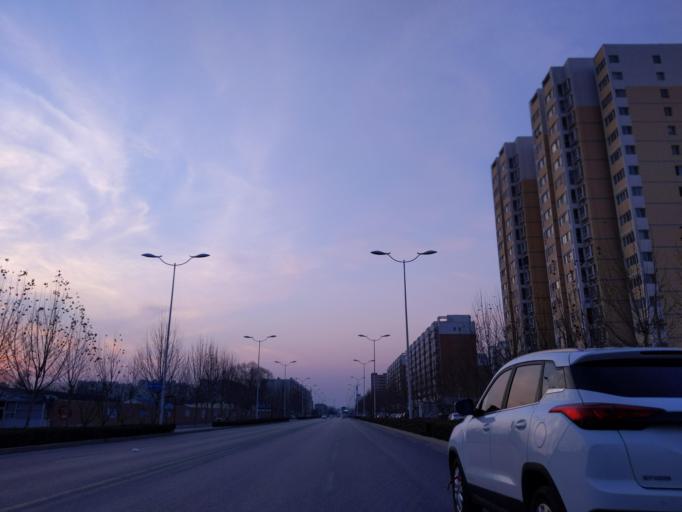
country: CN
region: Henan Sheng
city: Zhongyuanlu
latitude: 35.7752
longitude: 115.1062
